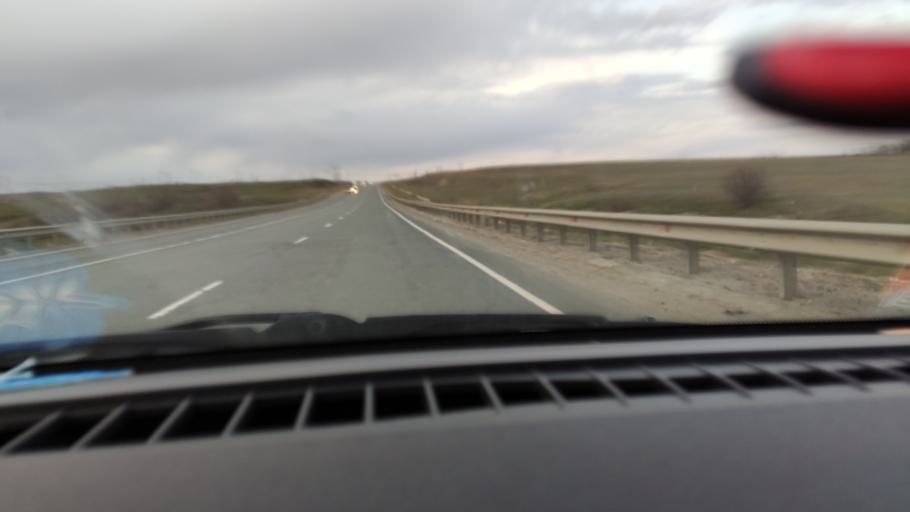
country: RU
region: Saratov
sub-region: Saratovskiy Rayon
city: Saratov
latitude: 51.7608
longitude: 46.0720
